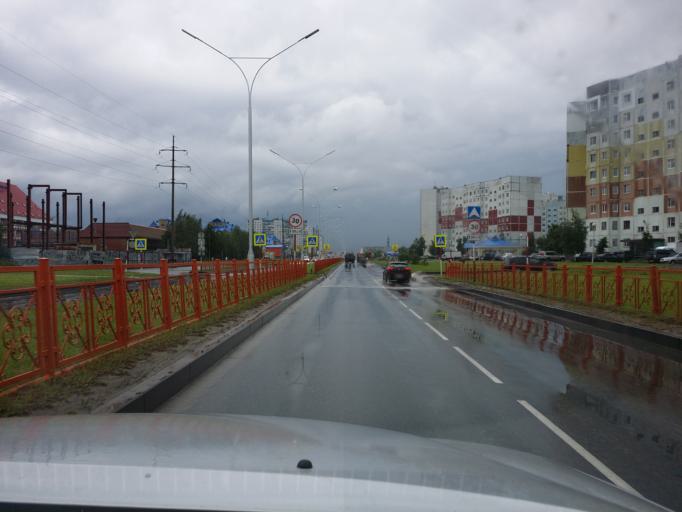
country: RU
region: Khanty-Mansiyskiy Avtonomnyy Okrug
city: Nizhnevartovsk
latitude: 60.9584
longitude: 76.5662
